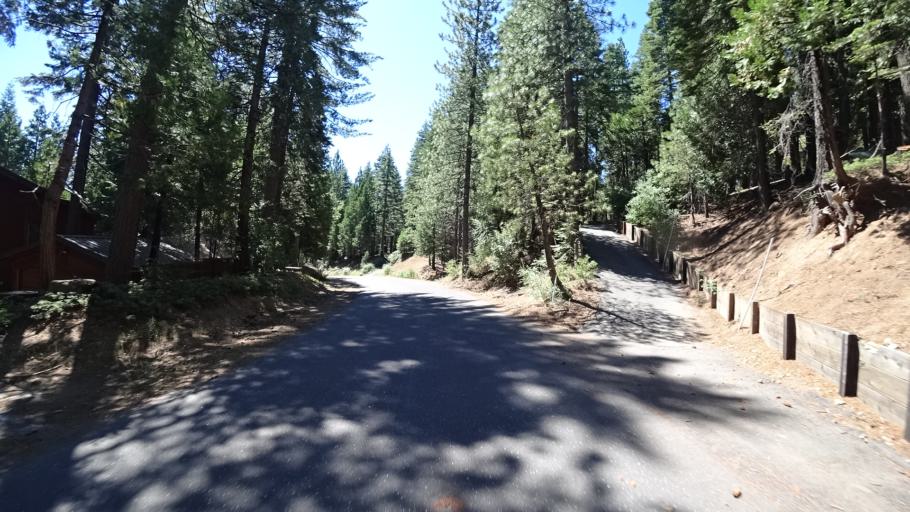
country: US
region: California
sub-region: Calaveras County
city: Arnold
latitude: 38.2876
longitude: -120.2868
